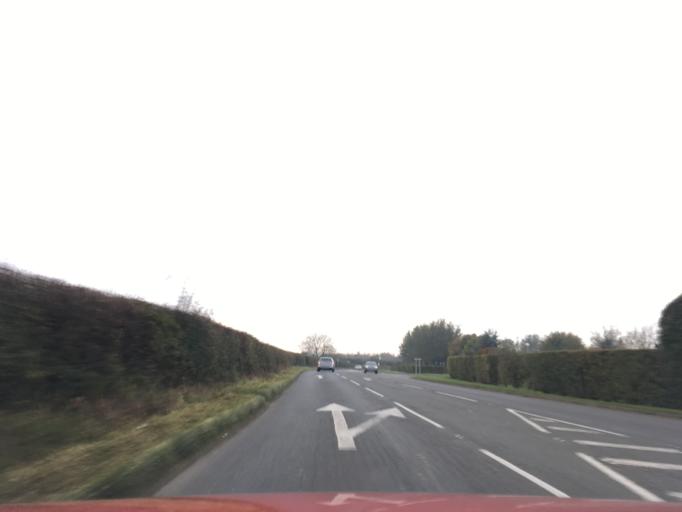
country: GB
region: England
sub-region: South Gloucestershire
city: Pucklechurch
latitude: 51.5053
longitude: -2.4275
